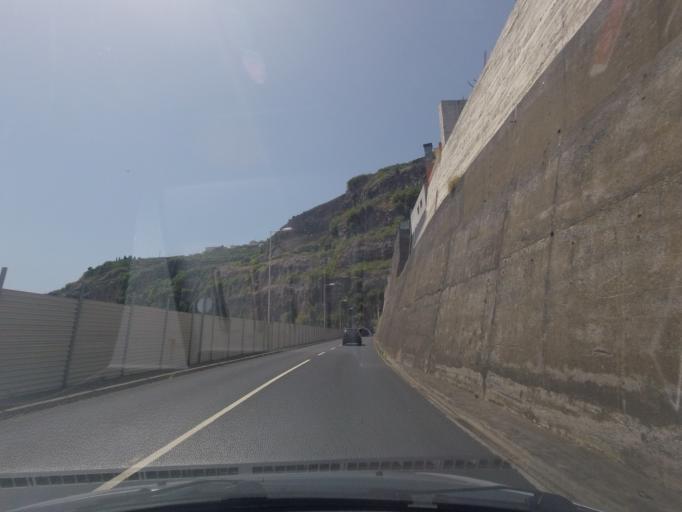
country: PT
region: Madeira
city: Ponta do Sol
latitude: 32.6800
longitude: -17.0928
